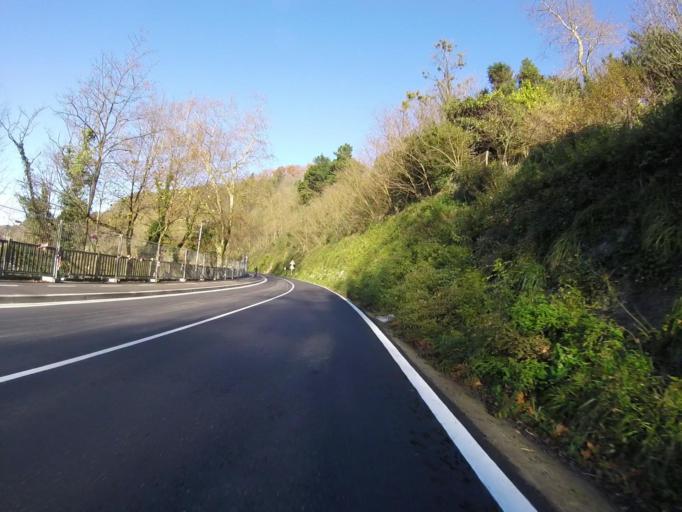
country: ES
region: Basque Country
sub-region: Provincia de Guipuzcoa
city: Lezo
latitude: 43.3237
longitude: -1.9009
